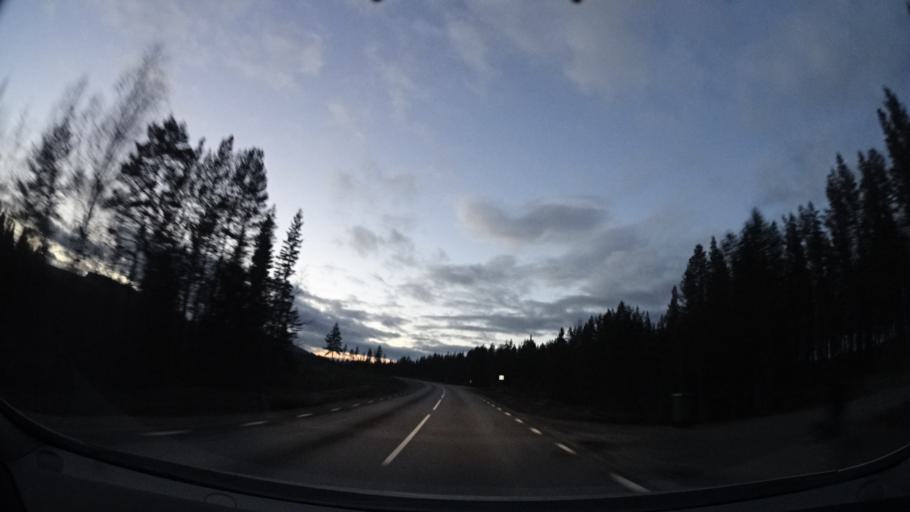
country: SE
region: Vaesterbotten
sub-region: Asele Kommun
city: Asele
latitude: 64.2006
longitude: 17.0558
